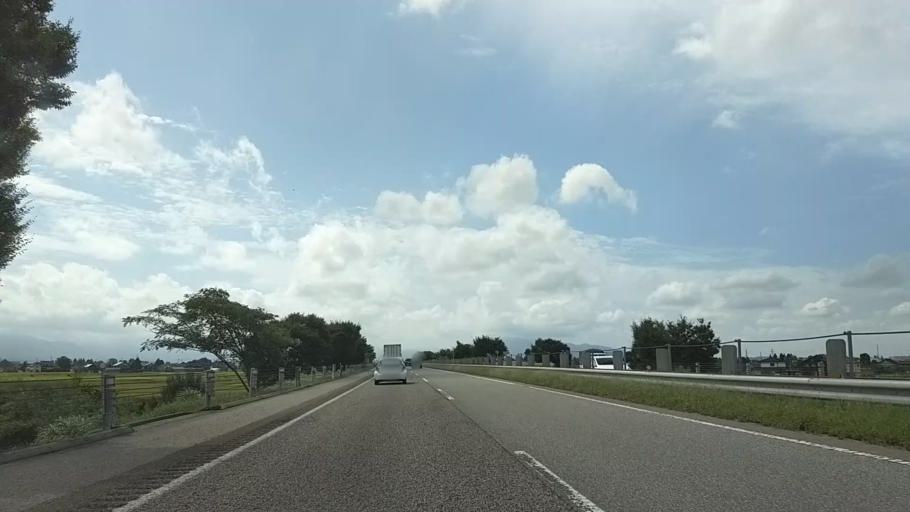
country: JP
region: Toyama
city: Nanto-shi
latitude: 36.6442
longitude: 136.9782
